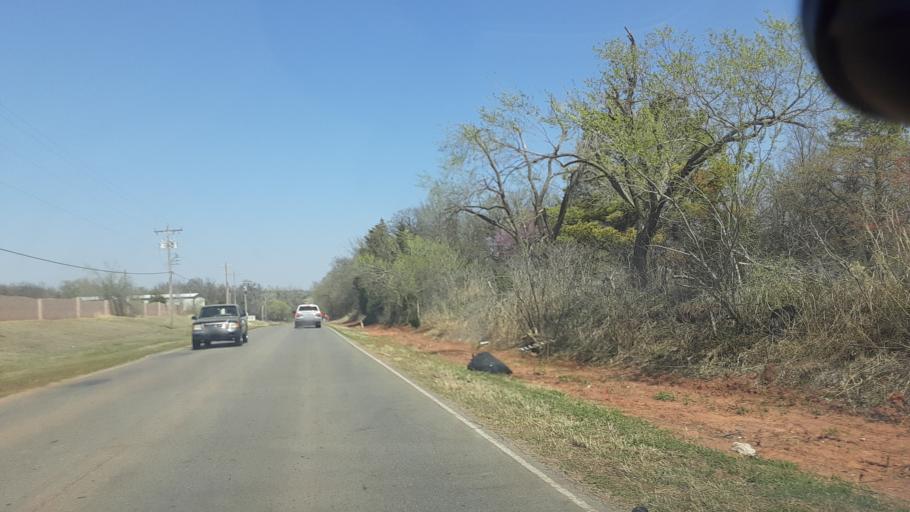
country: US
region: Oklahoma
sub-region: Oklahoma County
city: Edmond
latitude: 35.7339
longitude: -97.4784
